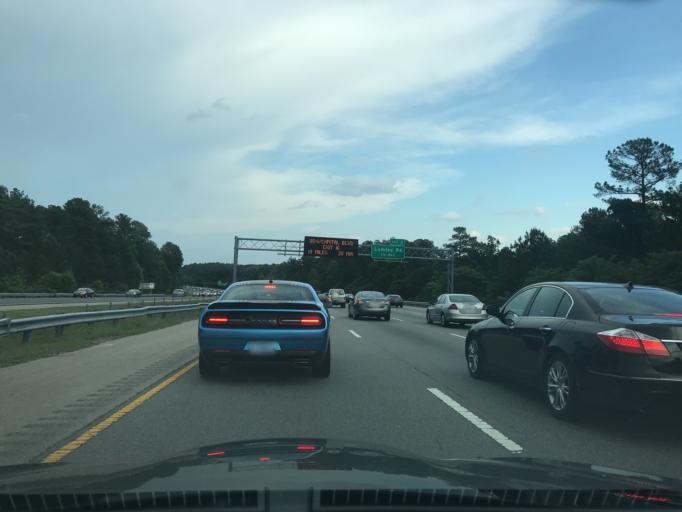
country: US
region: North Carolina
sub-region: Wake County
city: Morrisville
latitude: 35.8946
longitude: -78.7978
